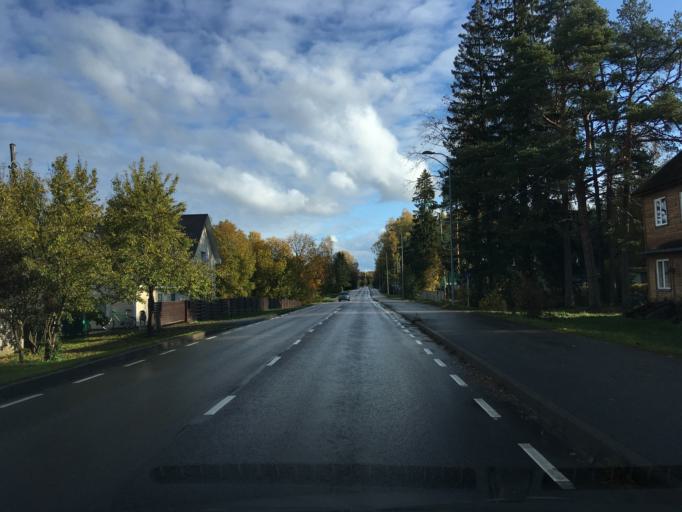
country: EE
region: Harju
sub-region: Raasiku vald
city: Raasiku
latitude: 59.1875
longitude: 25.1721
